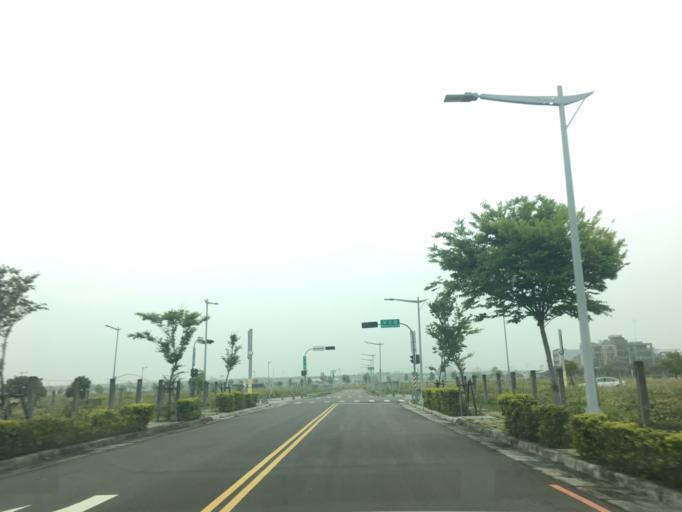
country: TW
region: Taiwan
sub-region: Taichung City
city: Taichung
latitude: 24.1927
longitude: 120.6756
